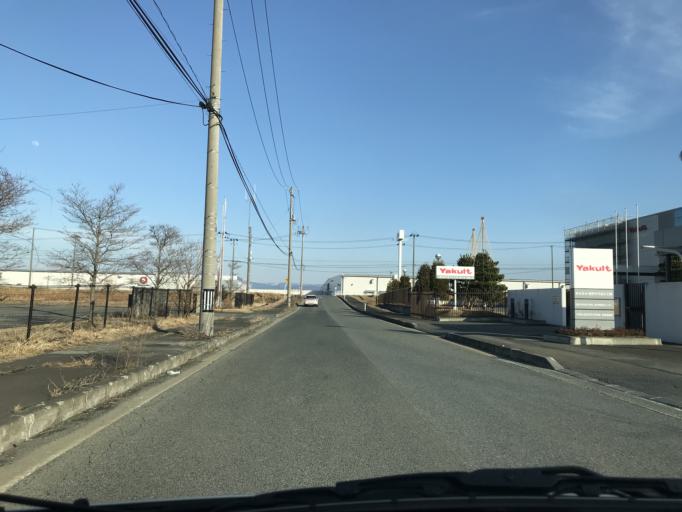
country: JP
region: Iwate
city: Kitakami
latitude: 39.2411
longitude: 141.0831
